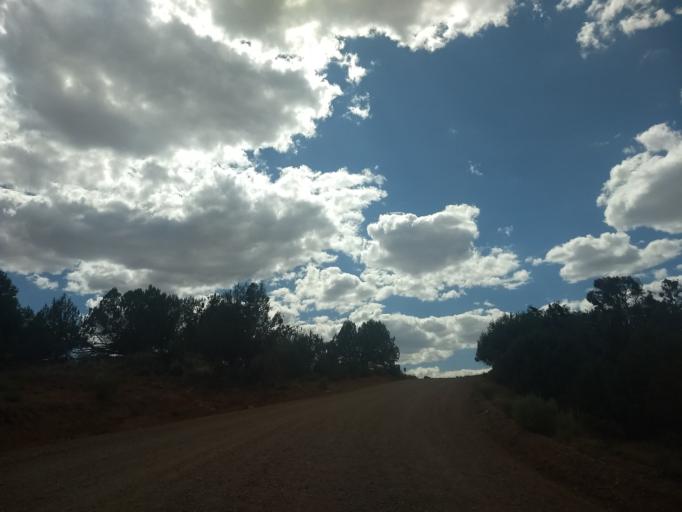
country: US
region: Utah
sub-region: Kane County
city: Kanab
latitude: 37.1472
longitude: -112.5465
